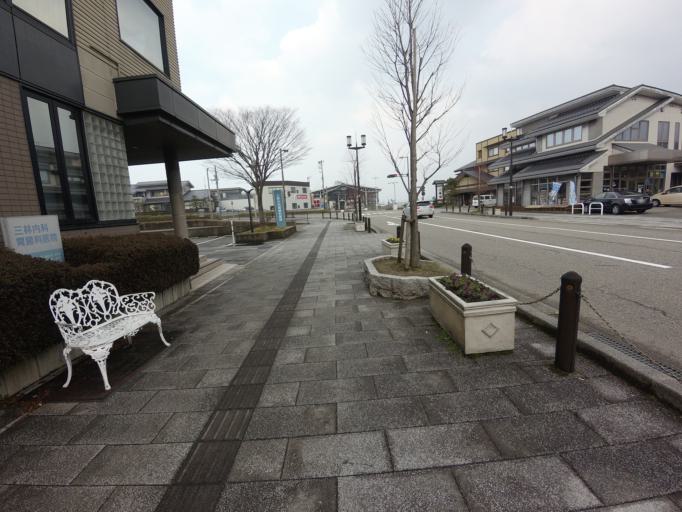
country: JP
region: Ishikawa
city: Nanao
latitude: 37.0477
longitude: 136.9674
